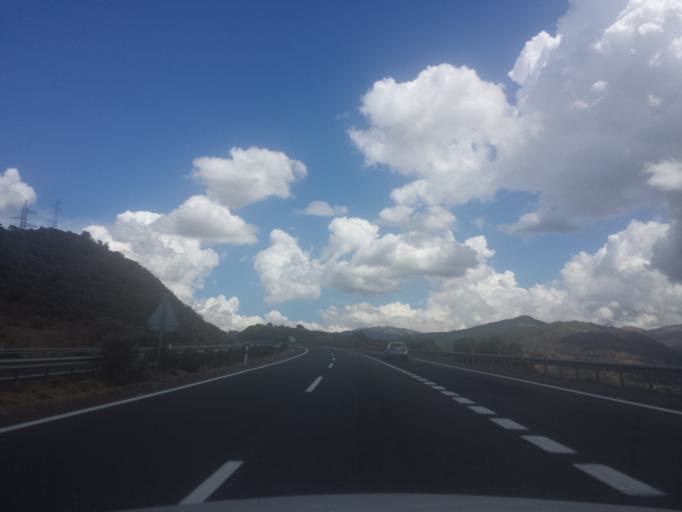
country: ES
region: Extremadura
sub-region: Provincia de Caceres
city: Aldeanueva del Camino
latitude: 40.2781
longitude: -5.9044
